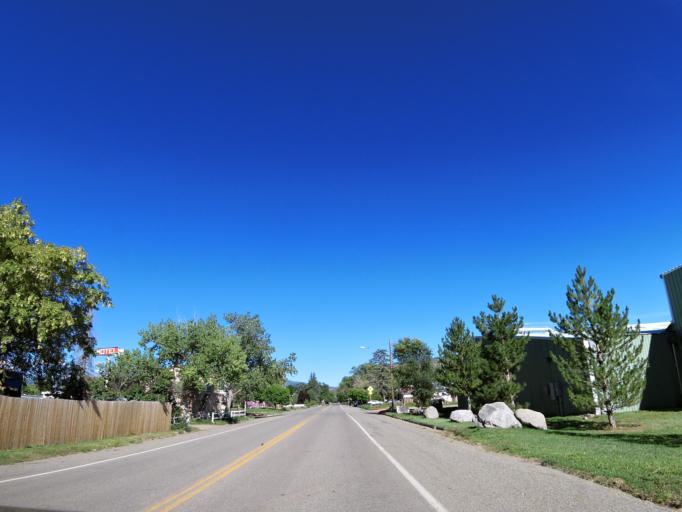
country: US
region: Colorado
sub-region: Montezuma County
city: Mancos
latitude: 37.3449
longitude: -108.3031
